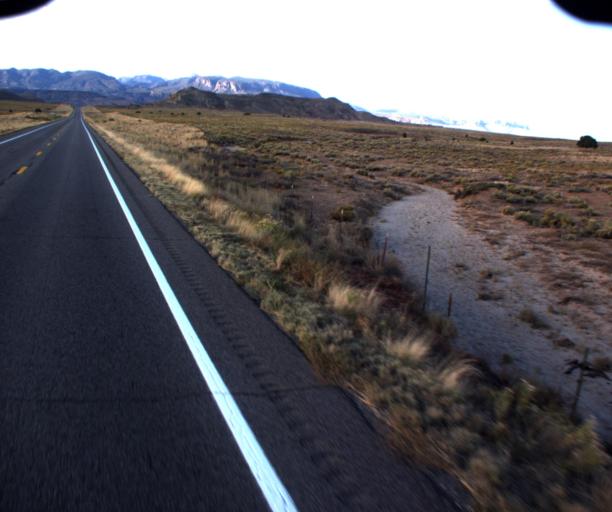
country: US
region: New Mexico
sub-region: San Juan County
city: Shiprock
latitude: 36.9585
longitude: -109.0675
